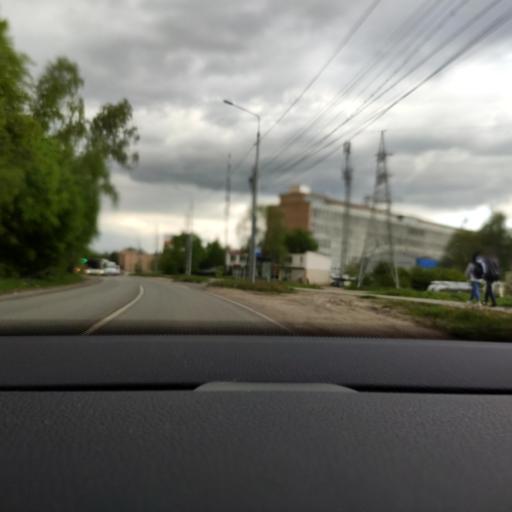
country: RU
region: Moskovskaya
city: Saltykovka
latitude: 55.7337
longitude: 37.9679
